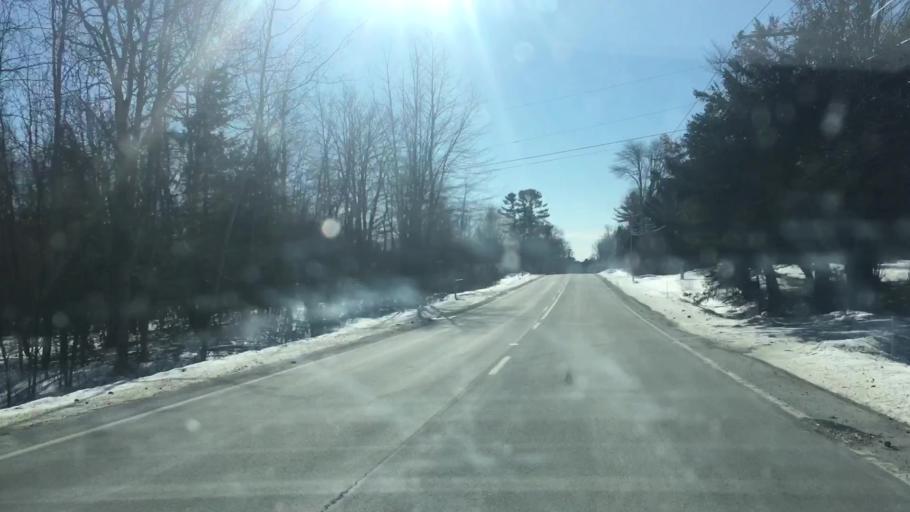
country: US
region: Maine
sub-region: Hancock County
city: Ellsworth
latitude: 44.5065
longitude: -68.4396
